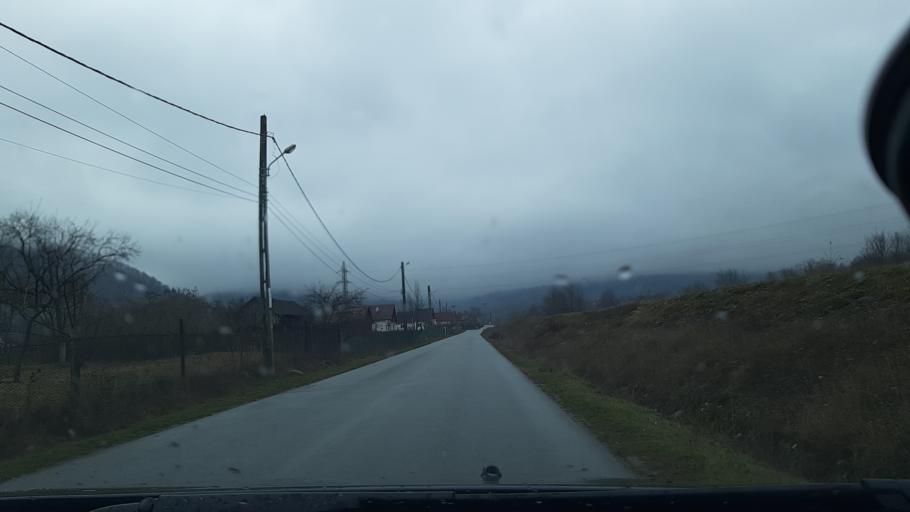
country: RO
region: Hunedoara
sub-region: Oras Petrila
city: Petrila
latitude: 45.4289
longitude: 23.4218
